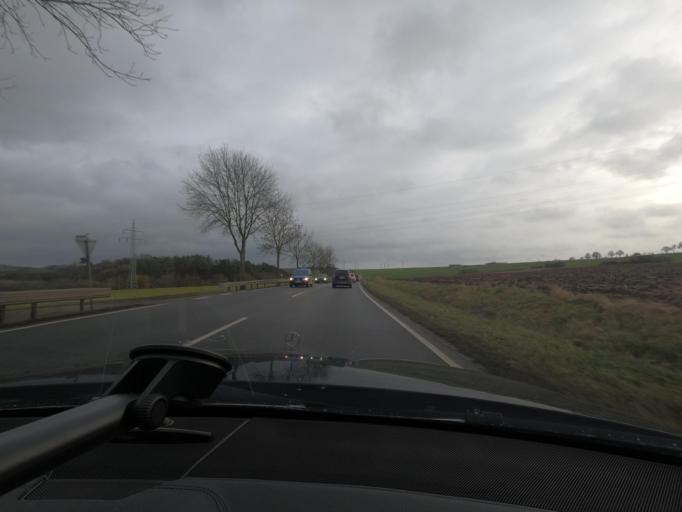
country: DE
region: Hesse
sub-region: Regierungsbezirk Kassel
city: Wolfhagen
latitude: 51.3163
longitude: 9.1906
